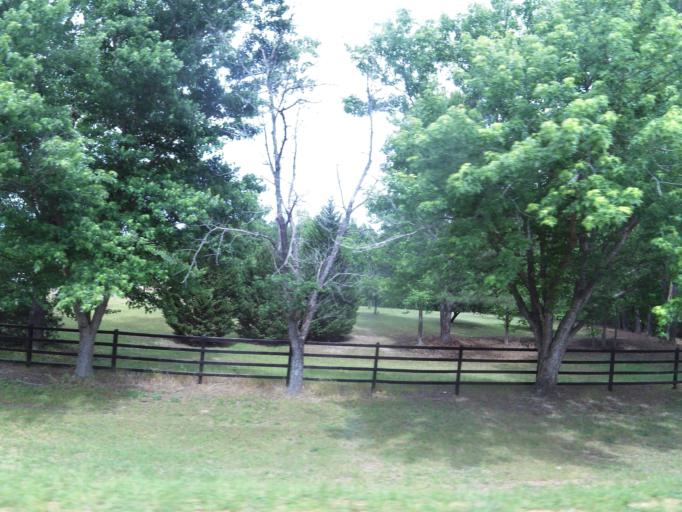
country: US
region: Georgia
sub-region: McDuffie County
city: Thomson
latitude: 33.3763
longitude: -82.4696
